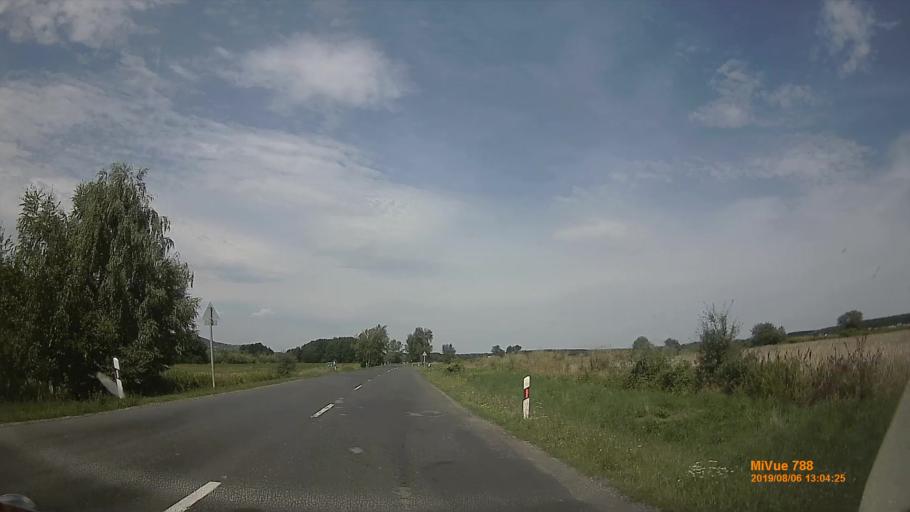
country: HU
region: Vas
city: Koszeg
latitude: 47.3522
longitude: 16.5691
